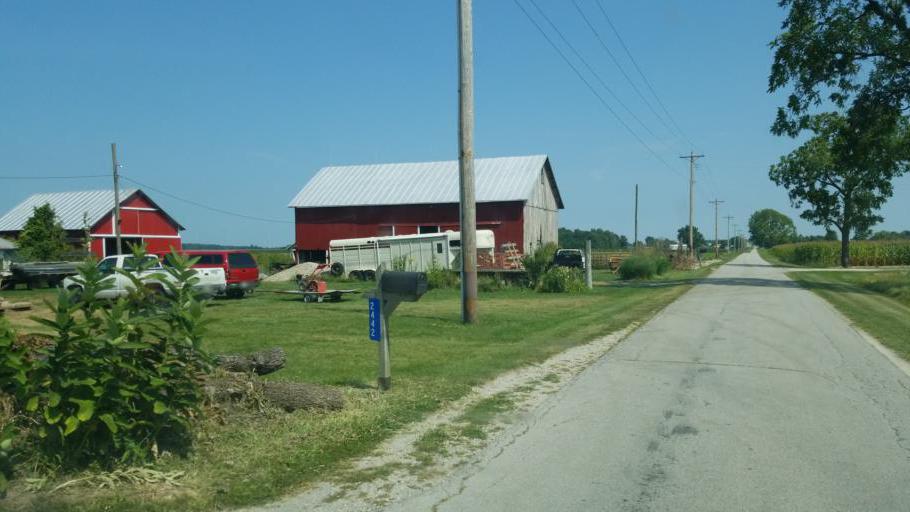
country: US
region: Ohio
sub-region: Crawford County
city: Bucyrus
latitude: 40.9358
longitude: -82.9952
